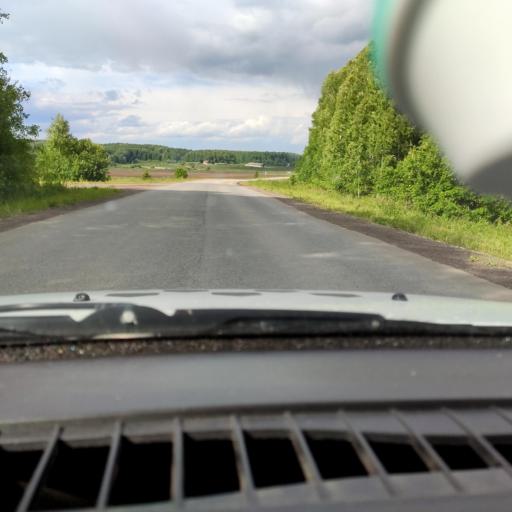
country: RU
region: Perm
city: Orda
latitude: 57.1738
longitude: 56.8266
